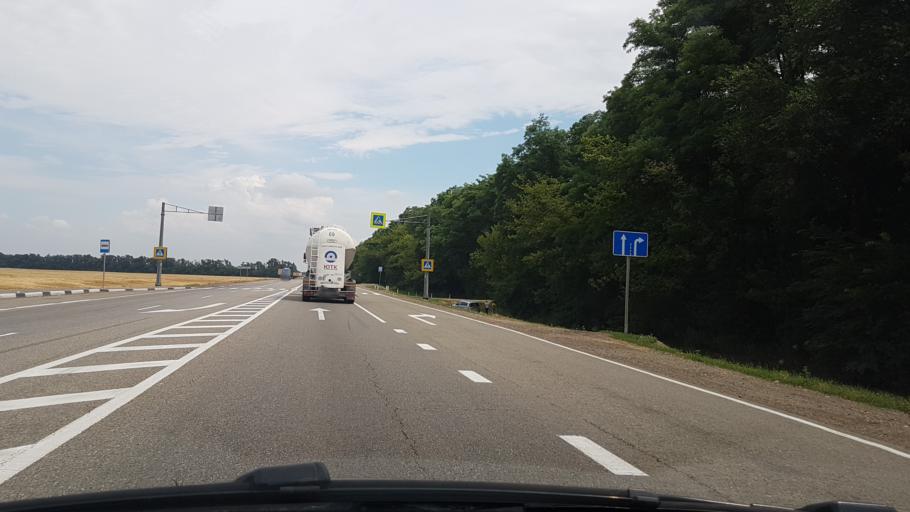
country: RU
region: Krasnodarskiy
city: Vasyurinskaya
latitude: 45.1651
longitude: 39.4693
